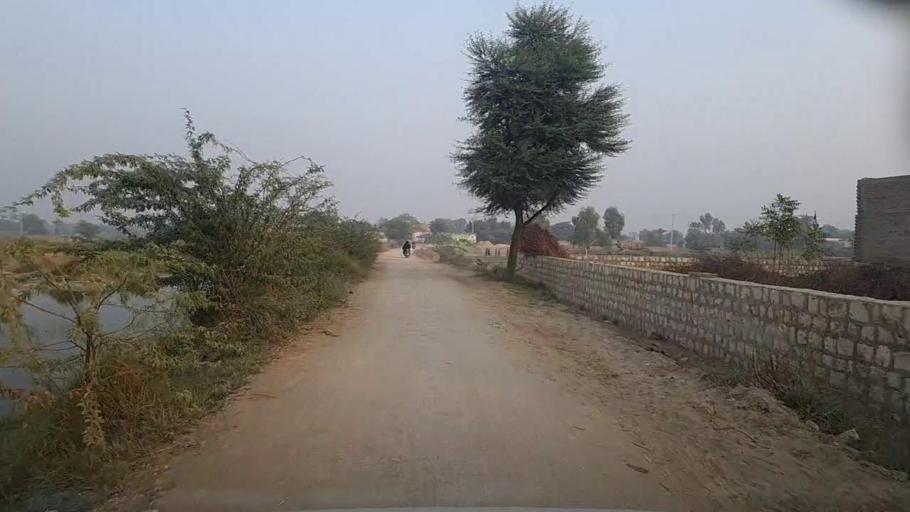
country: PK
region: Sindh
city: Bozdar
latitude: 27.0736
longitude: 68.5953
